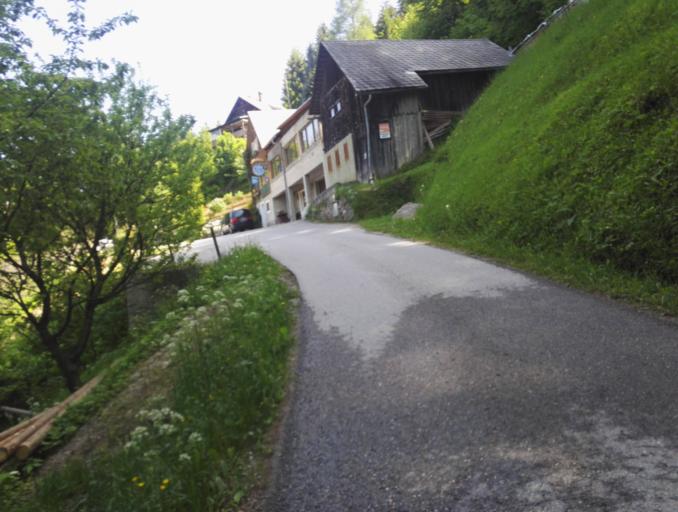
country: AT
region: Styria
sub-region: Politischer Bezirk Graz-Umgebung
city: Semriach
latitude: 47.1903
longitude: 15.4281
